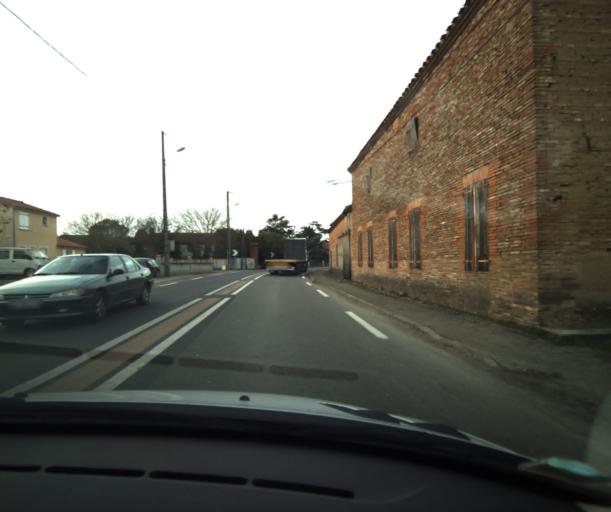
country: FR
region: Midi-Pyrenees
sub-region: Departement du Tarn-et-Garonne
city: Saint-Porquier
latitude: 44.0055
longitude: 1.1780
